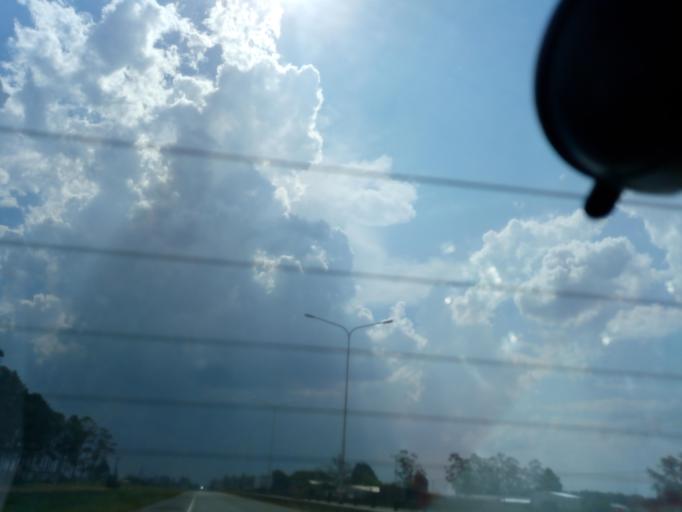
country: AR
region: Corrientes
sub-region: Departamento de Paso de los Libres
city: Paso de los Libres
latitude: -29.7220
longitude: -57.1636
